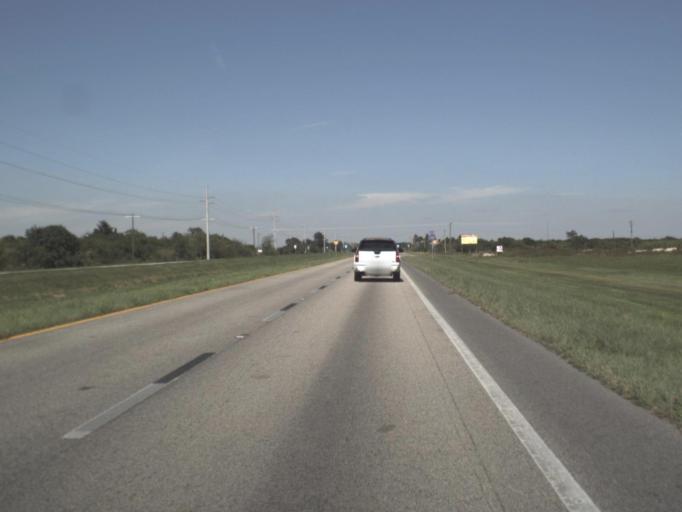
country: US
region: Florida
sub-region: Glades County
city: Moore Haven
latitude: 26.8087
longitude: -81.0824
